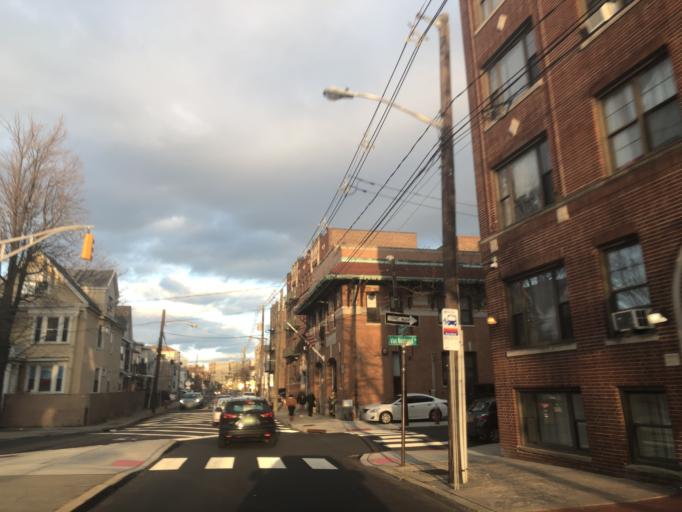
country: US
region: New Jersey
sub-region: Hudson County
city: Jersey City
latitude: 40.7036
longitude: -74.0902
